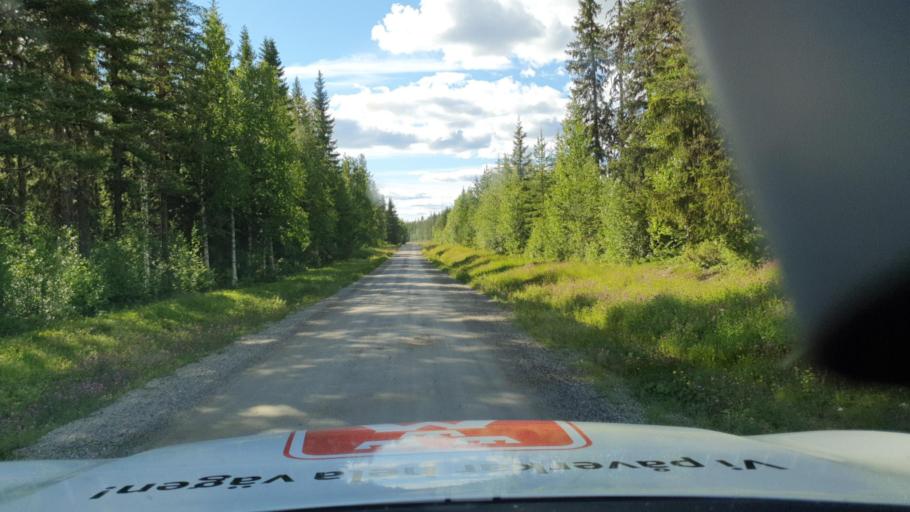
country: SE
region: Vaesterbotten
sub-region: Lycksele Kommun
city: Lycksele
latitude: 64.4080
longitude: 18.5083
